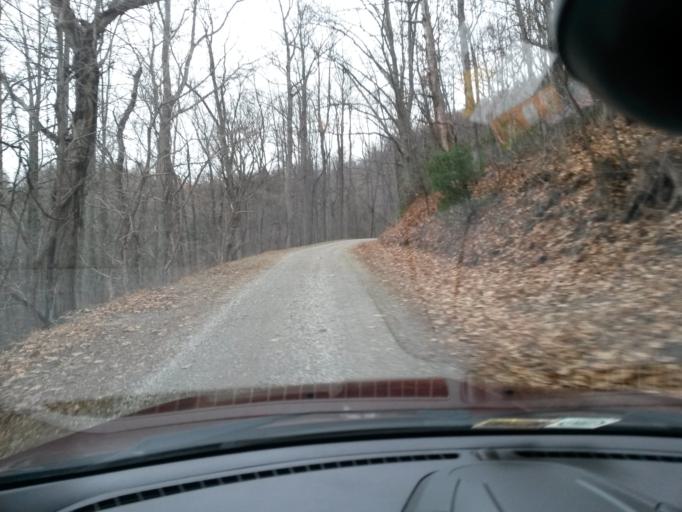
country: US
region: Virginia
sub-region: City of Buena Vista
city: Buena Vista
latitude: 37.7207
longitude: -79.2443
